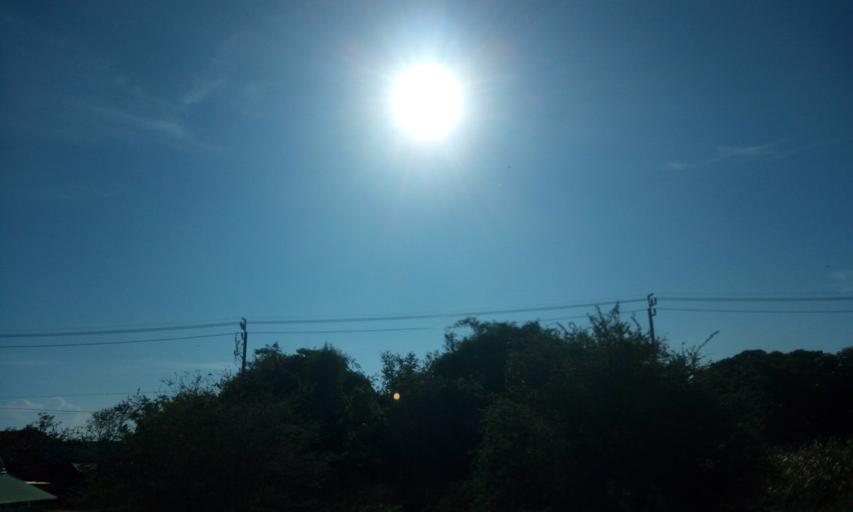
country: TH
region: Samut Prakan
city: Bang Bo District
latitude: 13.5282
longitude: 100.7482
